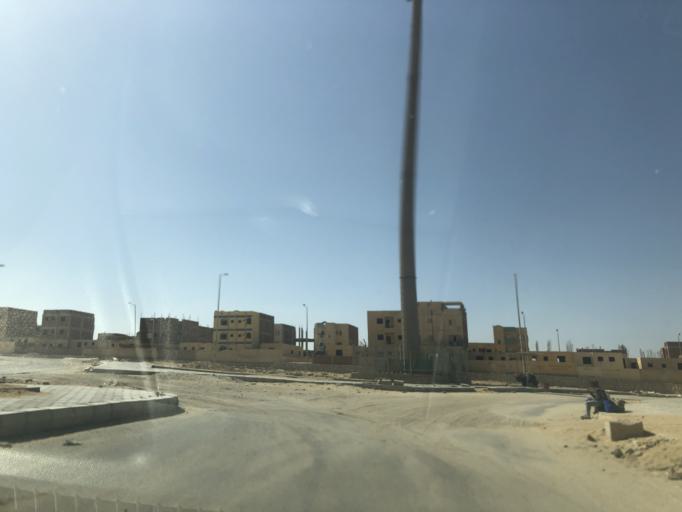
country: EG
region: Al Jizah
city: Madinat Sittah Uktubar
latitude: 29.9358
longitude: 30.9780
